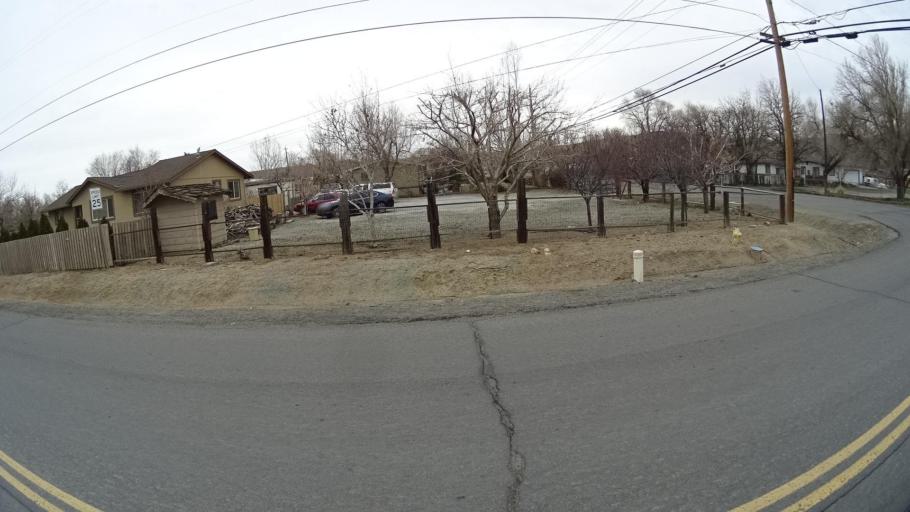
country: US
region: Nevada
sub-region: Washoe County
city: Sun Valley
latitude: 39.5930
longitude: -119.7711
